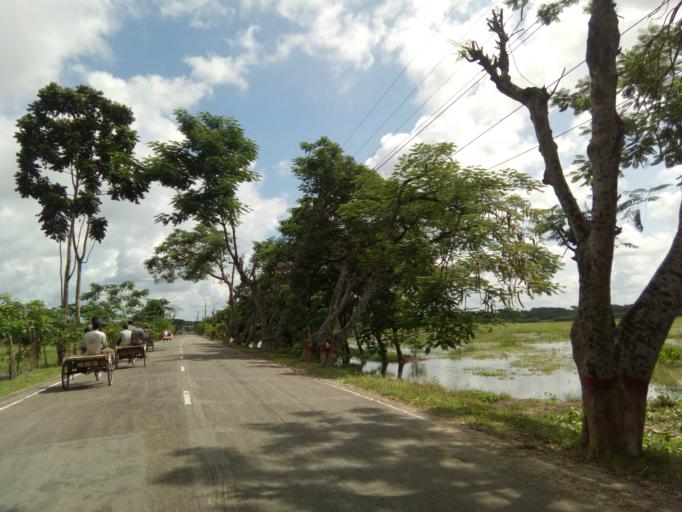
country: BD
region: Dhaka
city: Tungipara
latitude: 22.8996
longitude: 89.8961
